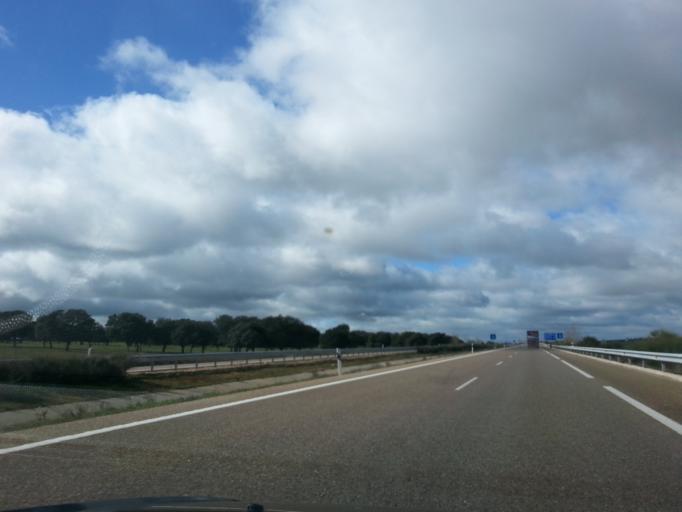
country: ES
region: Castille and Leon
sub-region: Provincia de Salamanca
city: Aldehuela de la Boveda
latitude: 40.8559
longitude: -6.0358
